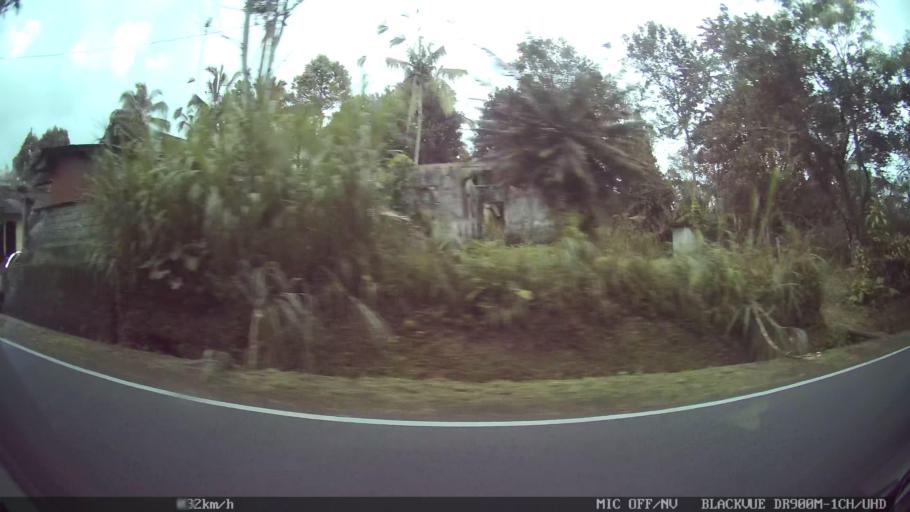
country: ID
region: Bali
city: Banjar Tiga
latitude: -8.3903
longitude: 115.4191
